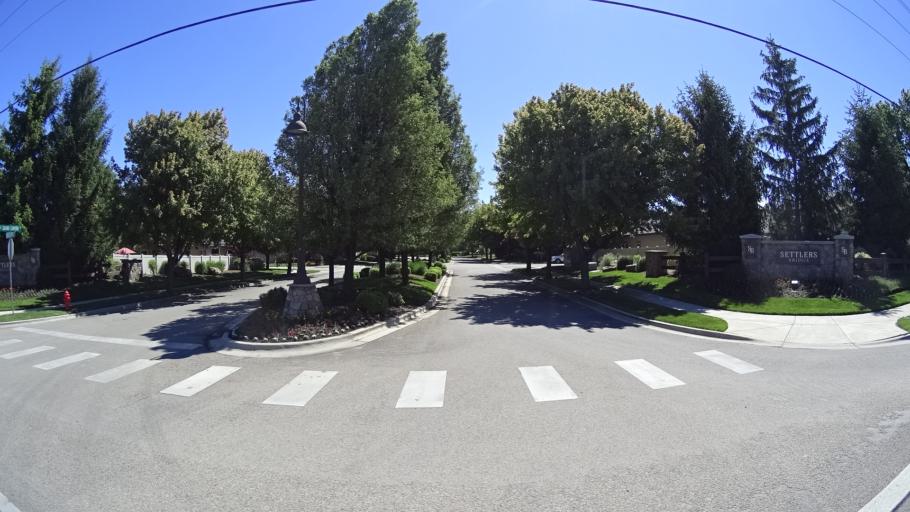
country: US
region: Idaho
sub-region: Ada County
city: Meridian
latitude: 43.6461
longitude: -116.3745
